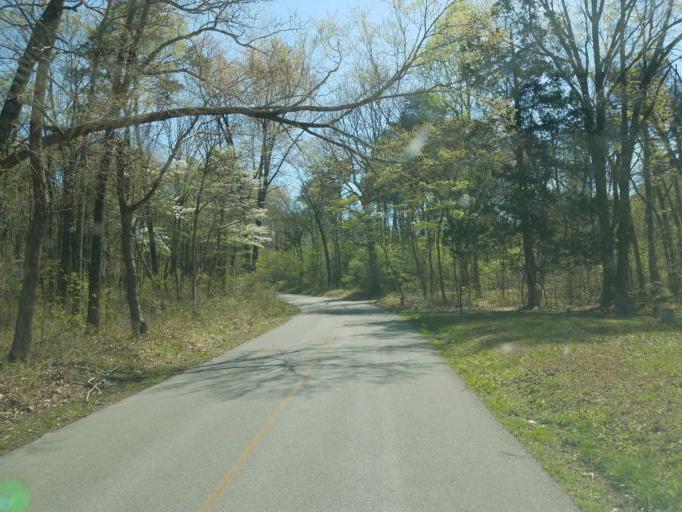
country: US
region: Kentucky
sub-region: Barren County
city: Cave City
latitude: 37.1959
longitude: -86.0597
